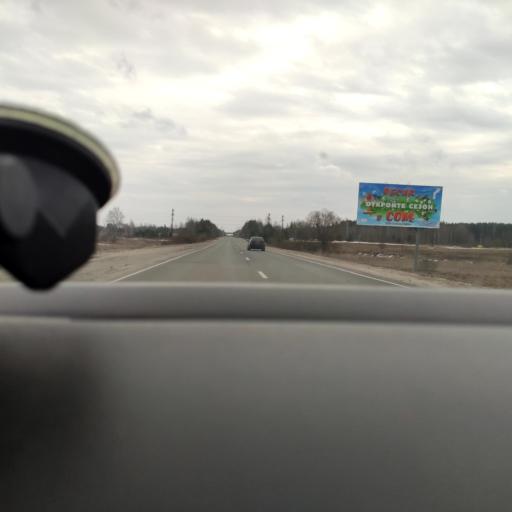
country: RU
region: Moskovskaya
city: Yegor'yevsk
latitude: 55.4237
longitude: 39.0374
